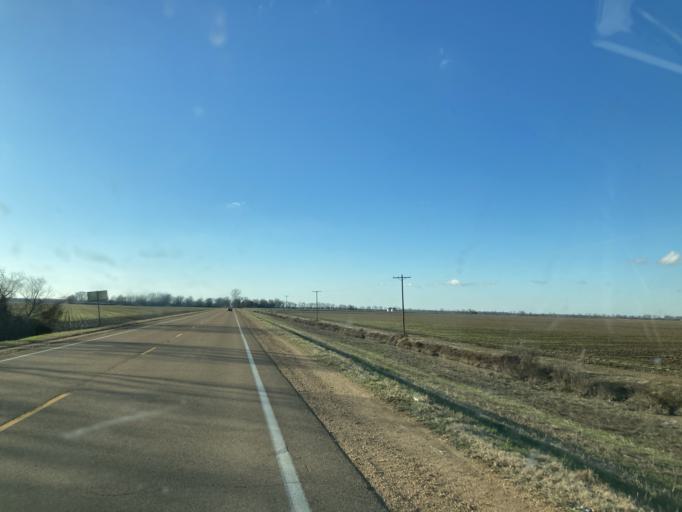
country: US
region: Mississippi
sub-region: Yazoo County
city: Yazoo City
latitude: 32.9253
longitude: -90.5752
